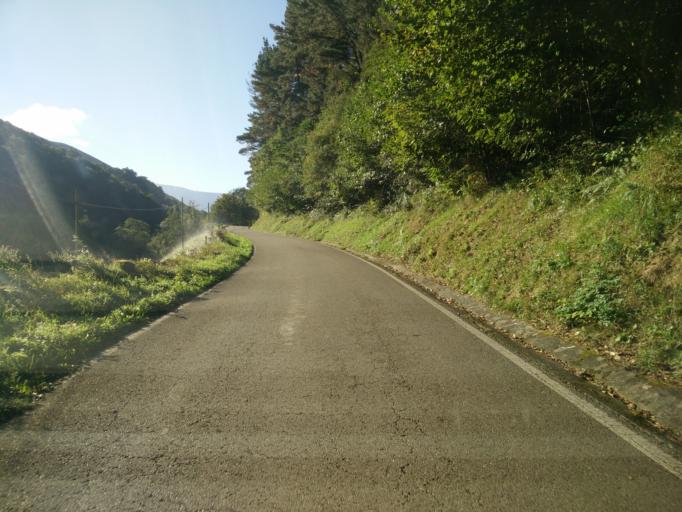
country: ES
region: Cantabria
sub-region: Provincia de Cantabria
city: Vega de Pas
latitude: 43.1581
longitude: -3.8223
